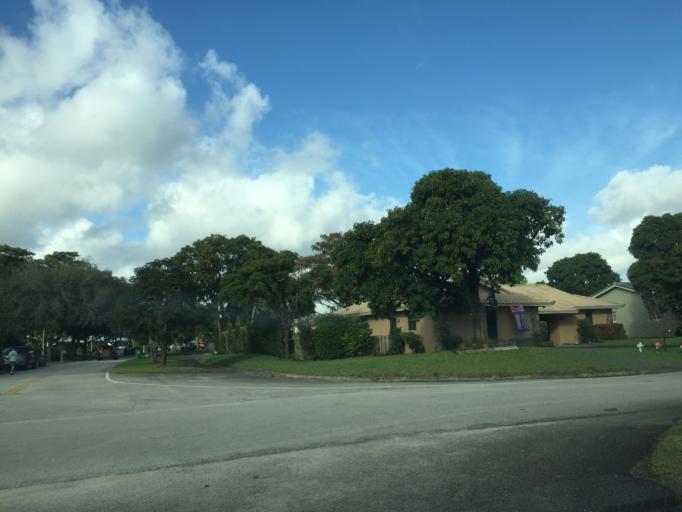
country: US
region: Florida
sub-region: Broward County
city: North Lauderdale
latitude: 26.2424
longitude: -80.2346
